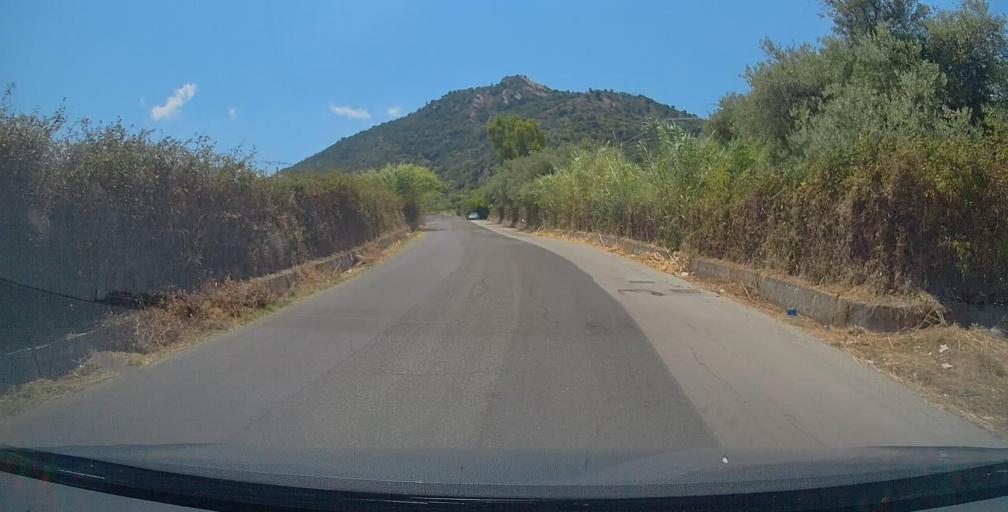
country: IT
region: Sicily
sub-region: Messina
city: Oliveri
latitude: 38.1428
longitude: 15.0157
